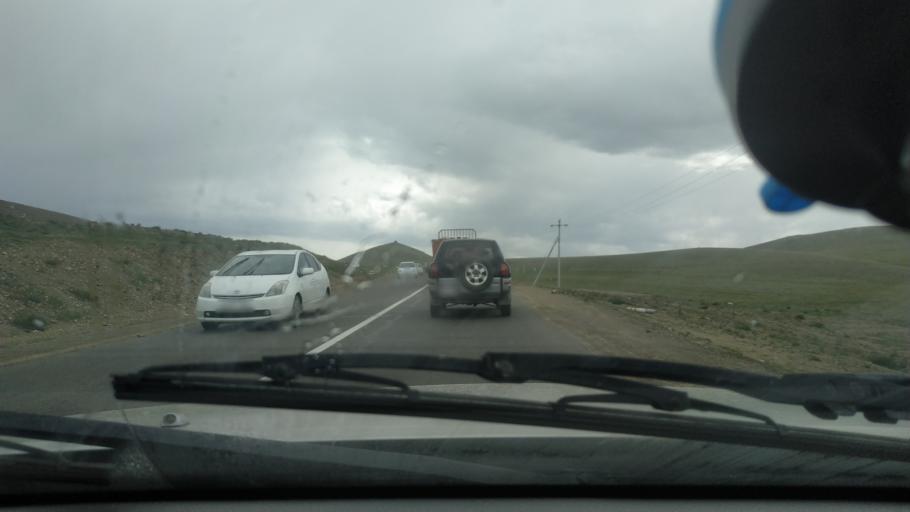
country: MN
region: Ulaanbaatar
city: Ulaanbaatar
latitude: 47.7941
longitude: 106.7452
